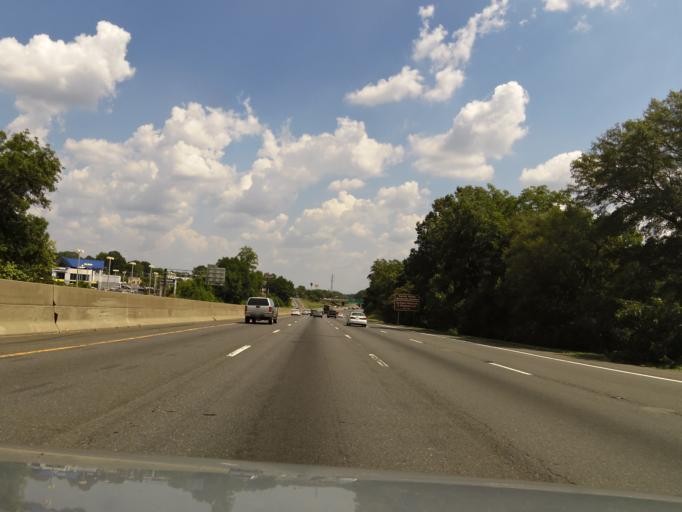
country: US
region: North Carolina
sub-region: Gaston County
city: Ranlo
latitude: 35.2711
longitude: -81.1550
